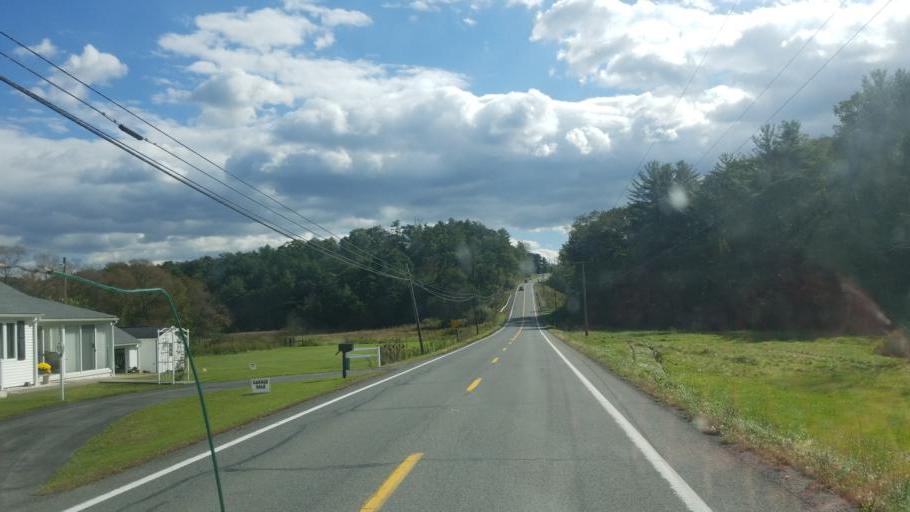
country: US
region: Pennsylvania
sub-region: Fulton County
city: McConnellsburg
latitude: 39.9956
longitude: -78.0925
